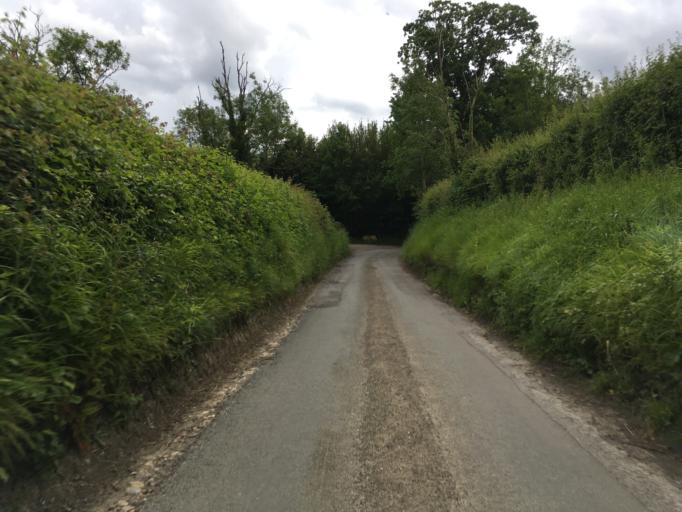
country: GB
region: England
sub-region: Wiltshire
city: Hankerton
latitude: 51.6449
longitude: -2.0138
